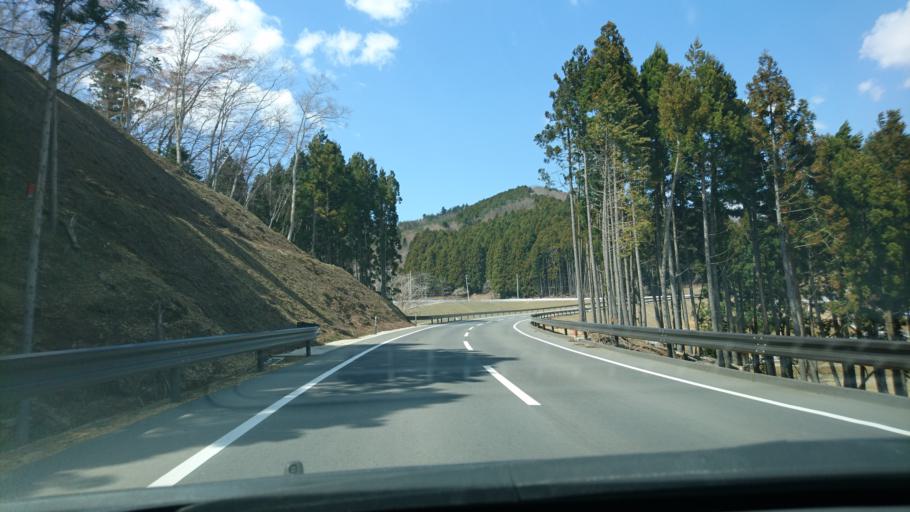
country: JP
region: Miyagi
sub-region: Oshika Gun
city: Onagawa Cho
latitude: 38.4630
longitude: 141.4741
